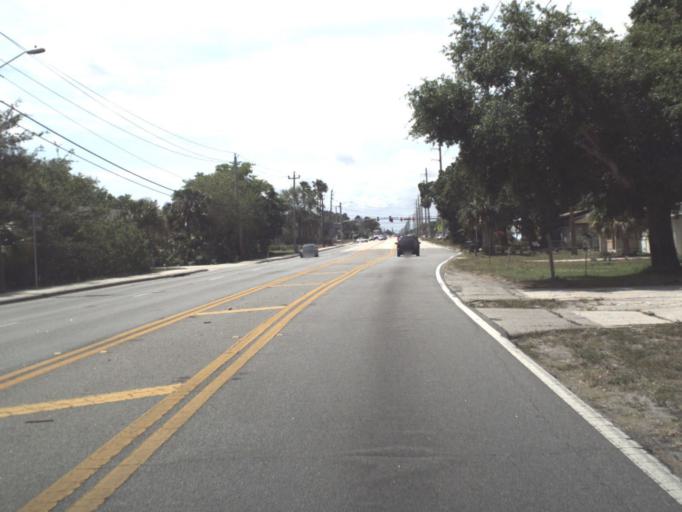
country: US
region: Florida
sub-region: Brevard County
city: Cocoa
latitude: 28.3911
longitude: -80.7551
